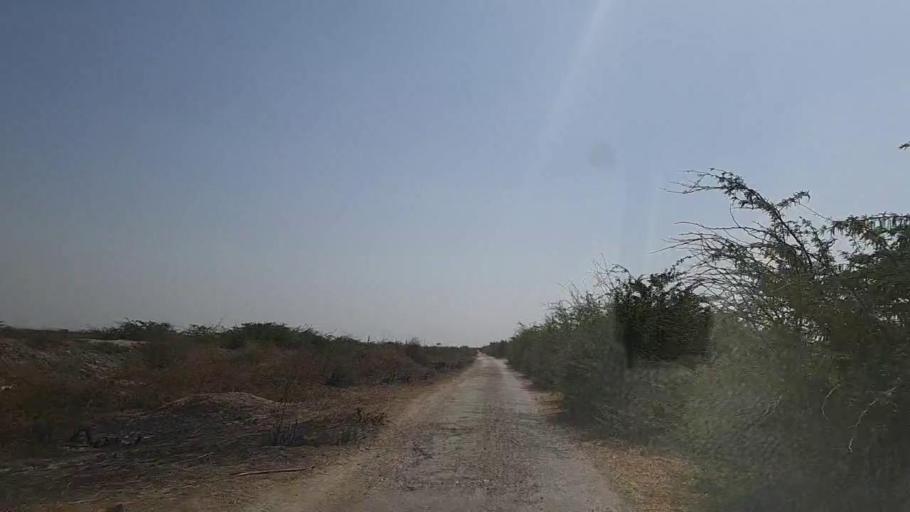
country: PK
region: Sindh
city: Naukot
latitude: 24.6281
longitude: 69.2710
